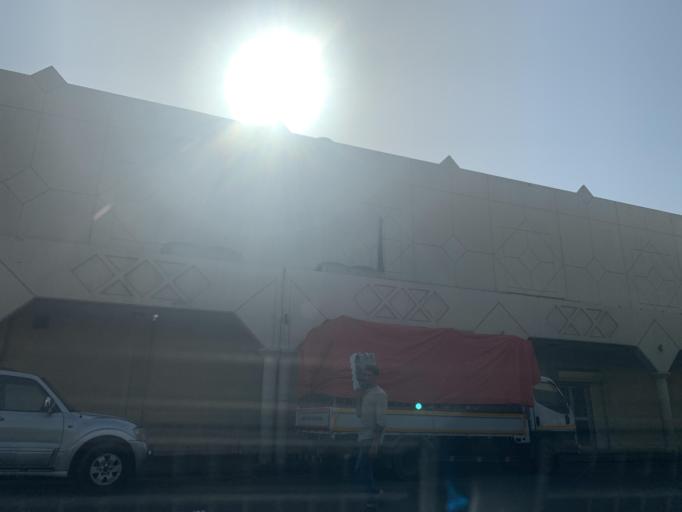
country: BH
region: Manama
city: Jidd Hafs
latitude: 26.2298
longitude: 50.5644
